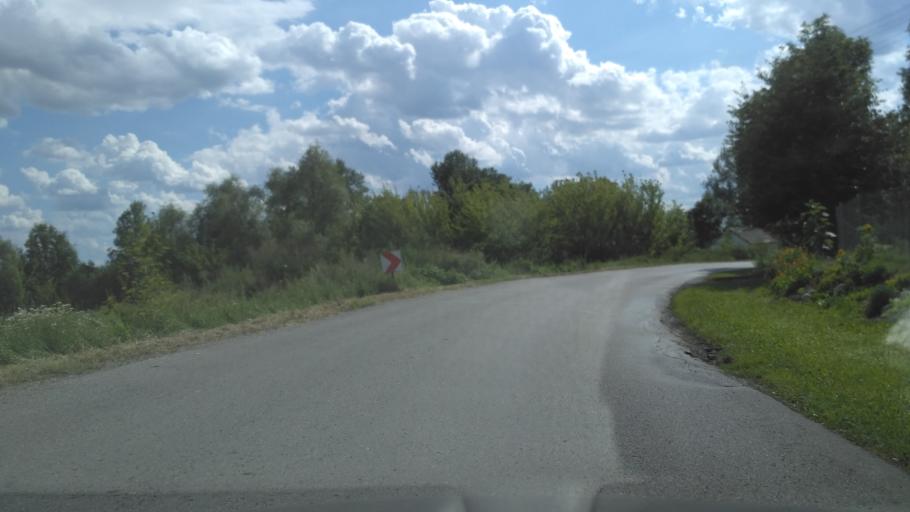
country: PL
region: Lublin Voivodeship
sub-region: Powiat leczynski
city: Milejow
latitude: 51.2147
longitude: 22.8894
